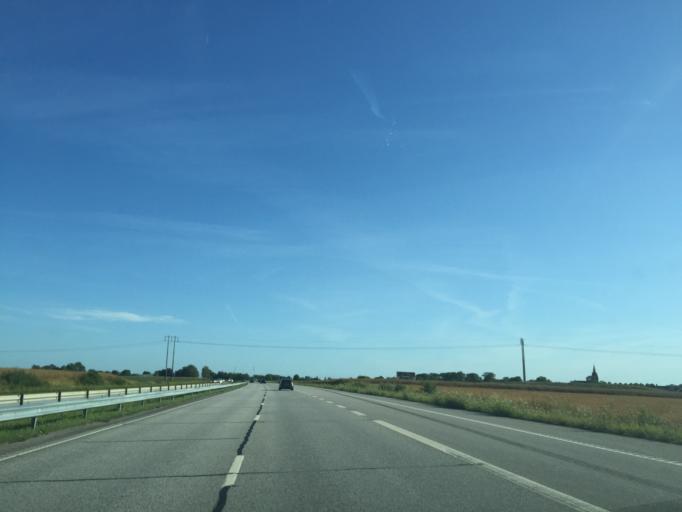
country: SE
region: Skane
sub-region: Malmo
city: Tygelsjo
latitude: 55.5258
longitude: 13.0077
